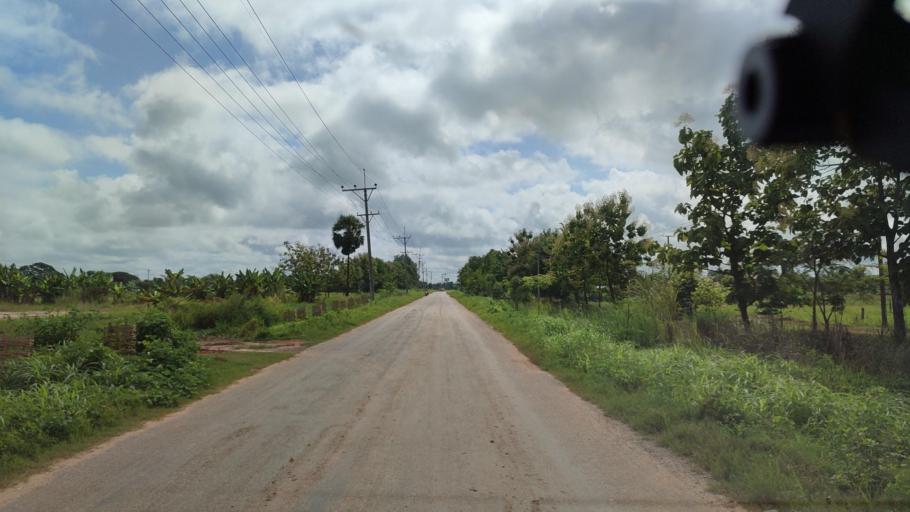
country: MM
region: Bago
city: Letpandan
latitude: 17.8949
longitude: 95.7310
